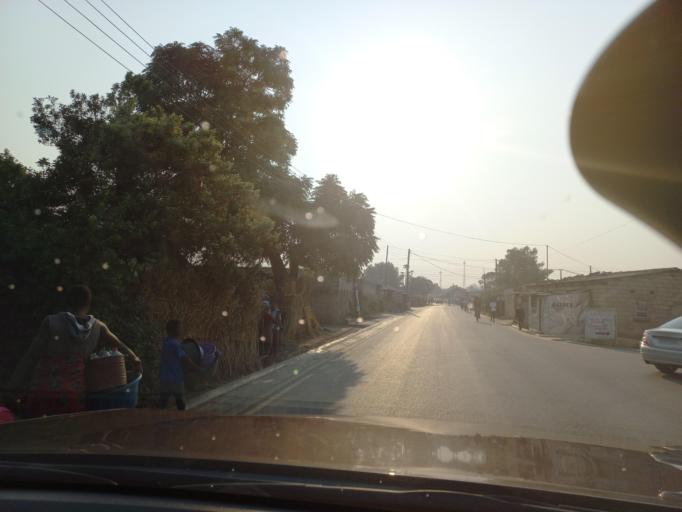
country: ZM
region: Lusaka
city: Lusaka
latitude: -15.4038
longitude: 28.3422
